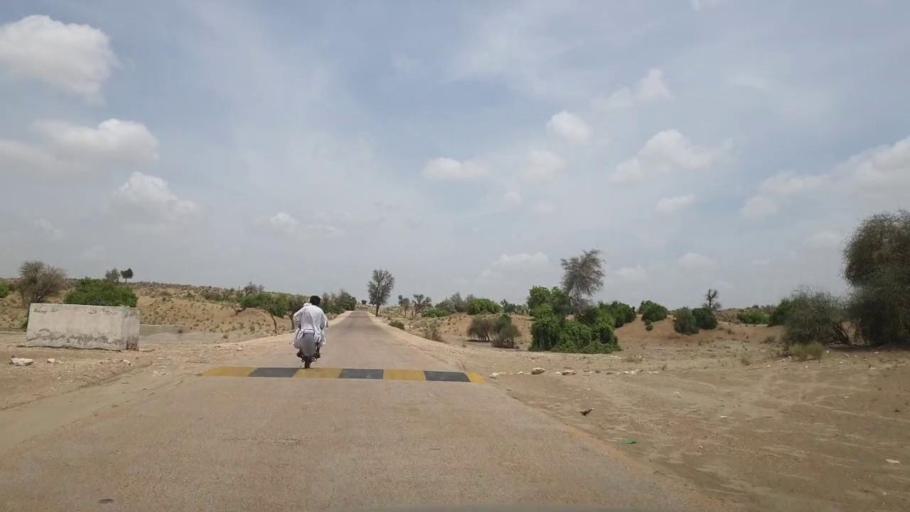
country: PK
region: Sindh
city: Kot Diji
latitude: 27.1809
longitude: 69.1784
